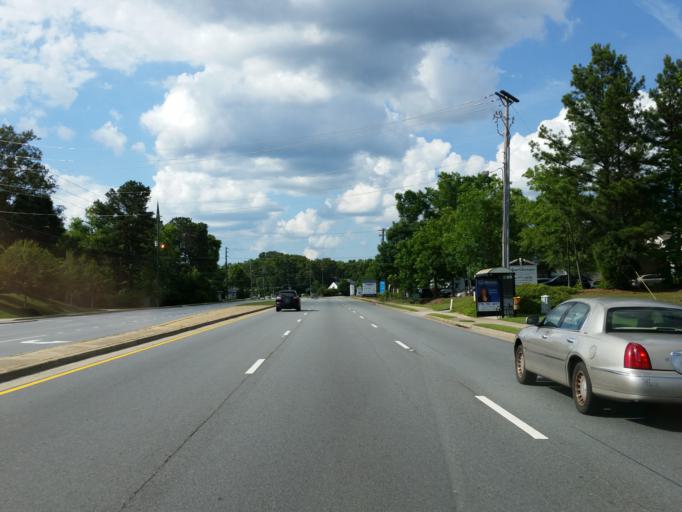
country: US
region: Georgia
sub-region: Fulton County
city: Sandy Springs
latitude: 33.9698
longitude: -84.4134
